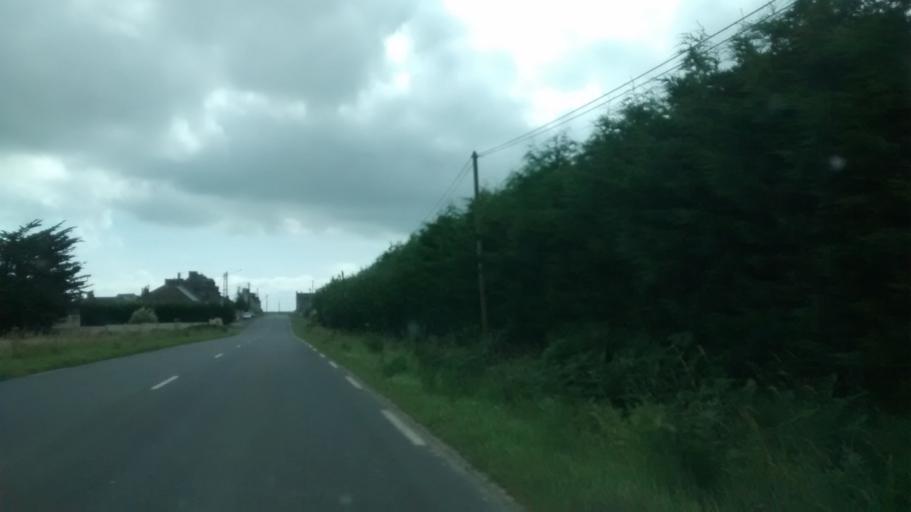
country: FR
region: Brittany
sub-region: Departement d'Ille-et-Vilaine
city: Saint-Meloir-des-Ondes
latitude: 48.6471
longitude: -1.9016
